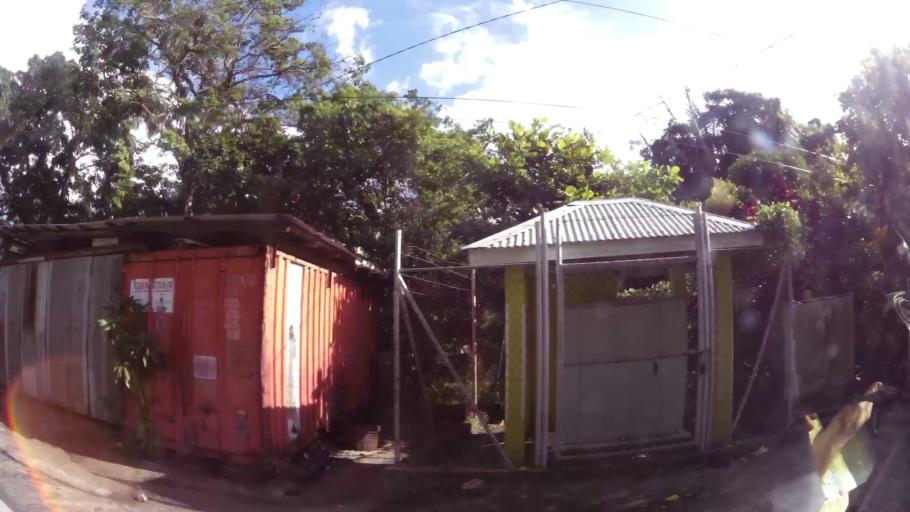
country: DM
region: Saint George
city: Roseau
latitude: 15.3037
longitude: -61.3750
